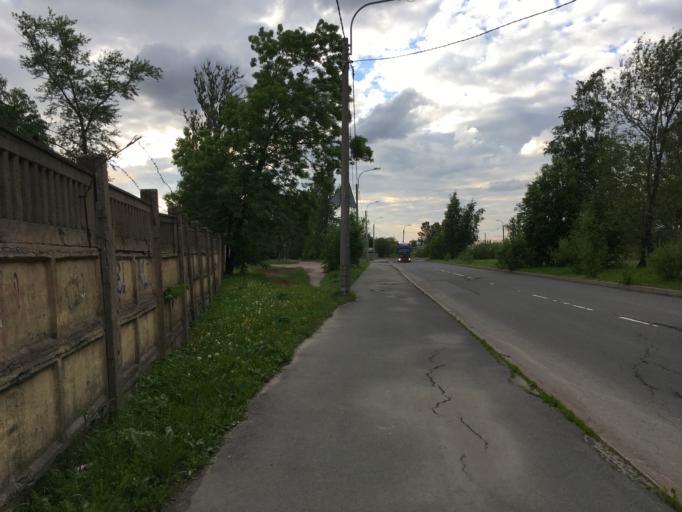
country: RU
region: St.-Petersburg
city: Centralniy
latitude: 59.9042
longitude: 30.3750
